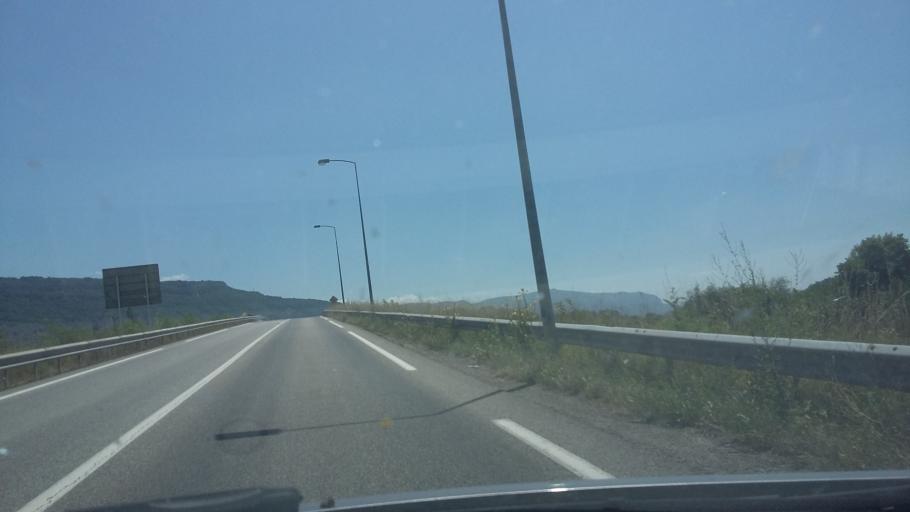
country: FR
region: Rhone-Alpes
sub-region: Departement de l'Ain
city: Belley
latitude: 45.7561
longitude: 5.7071
